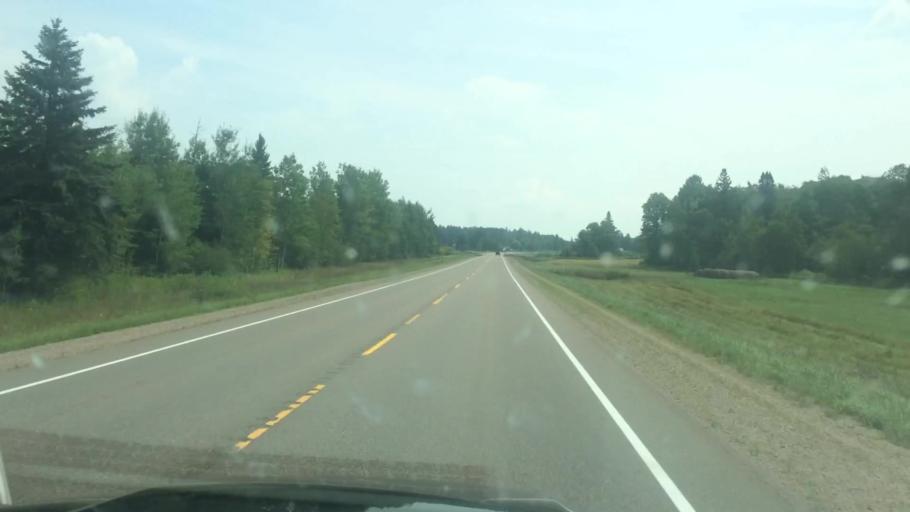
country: US
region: Wisconsin
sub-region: Langlade County
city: Antigo
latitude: 45.1458
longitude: -89.2858
